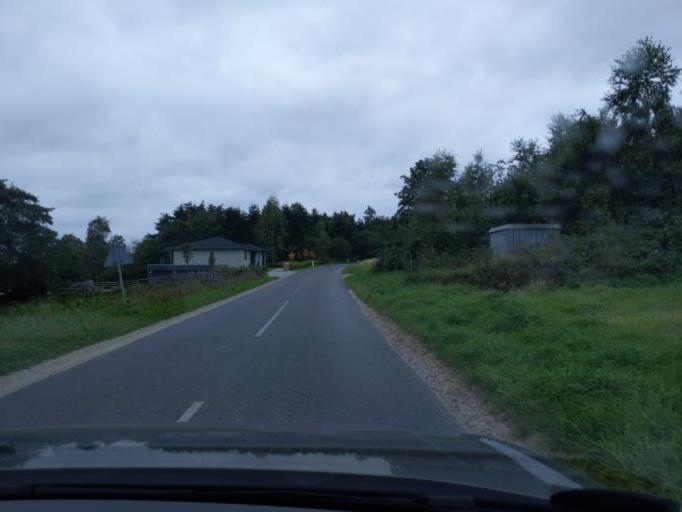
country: DK
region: North Denmark
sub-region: Mariagerfjord Kommune
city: Hobro
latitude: 56.5606
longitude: 9.7082
